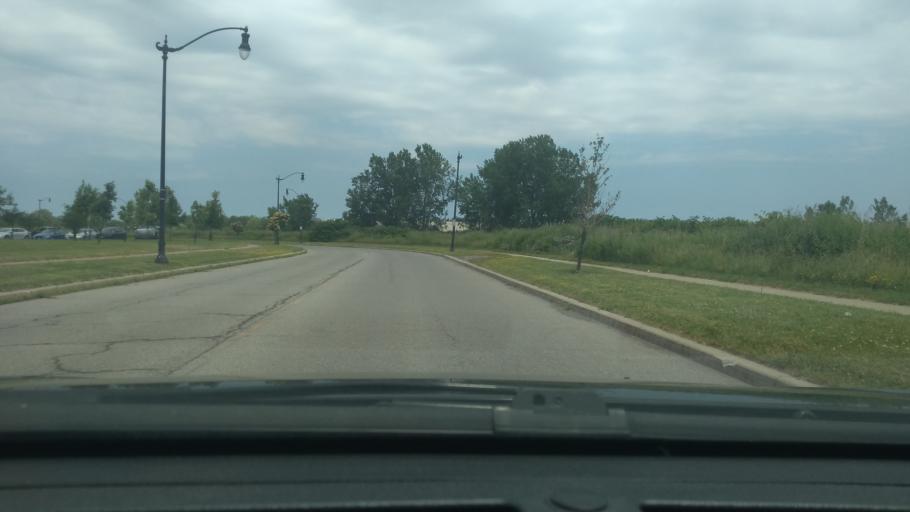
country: US
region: New York
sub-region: Erie County
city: Lackawanna
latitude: 42.8363
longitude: -78.8458
